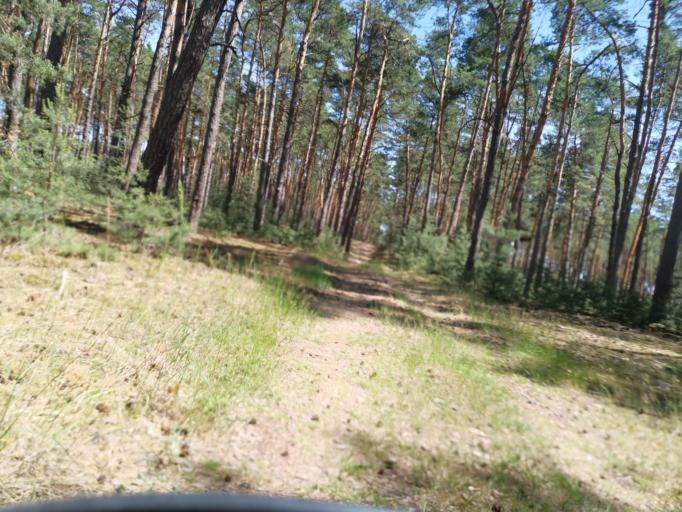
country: CZ
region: South Moravian
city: Bzenec
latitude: 48.9375
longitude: 17.2564
